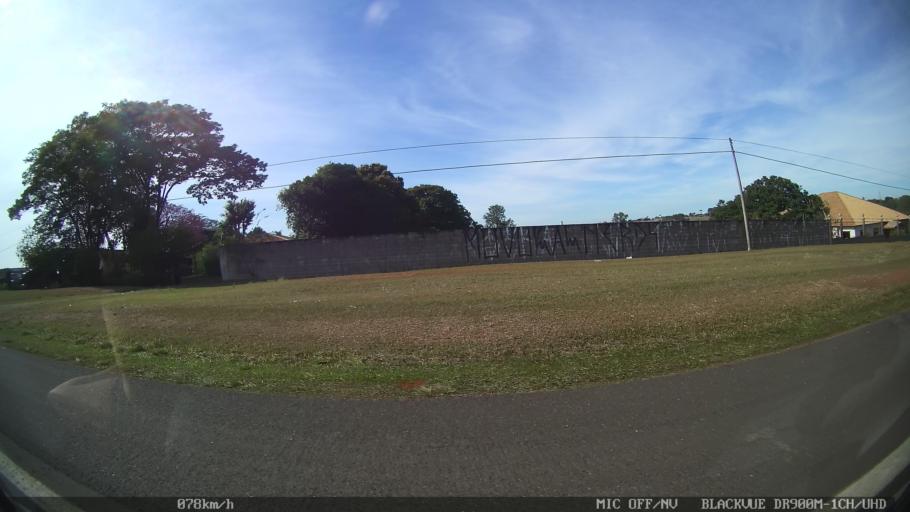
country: BR
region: Sao Paulo
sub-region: Piracicaba
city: Piracicaba
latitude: -22.7694
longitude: -47.6472
